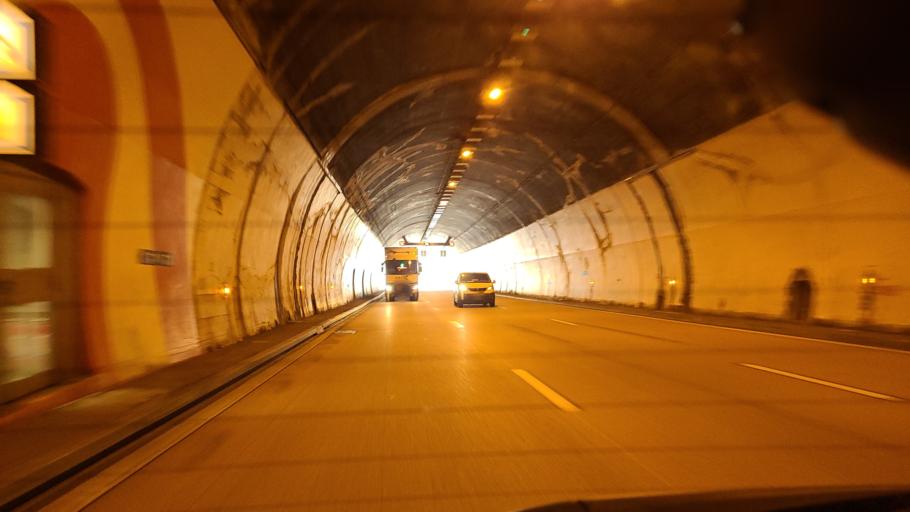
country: MC
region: Commune de Monaco
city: Saint-Roman
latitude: 43.7590
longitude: 7.4357
